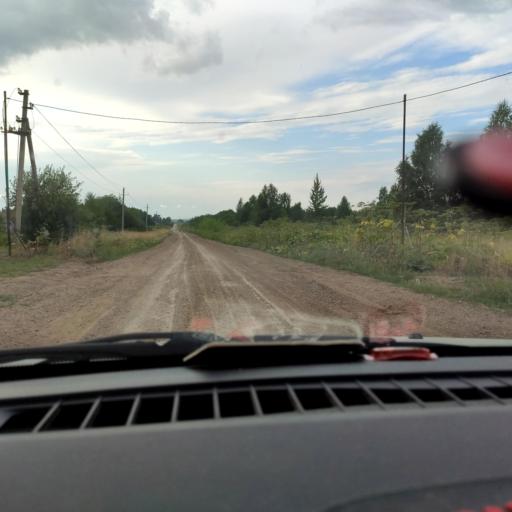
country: RU
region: Perm
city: Kultayevo
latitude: 57.8225
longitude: 55.9979
